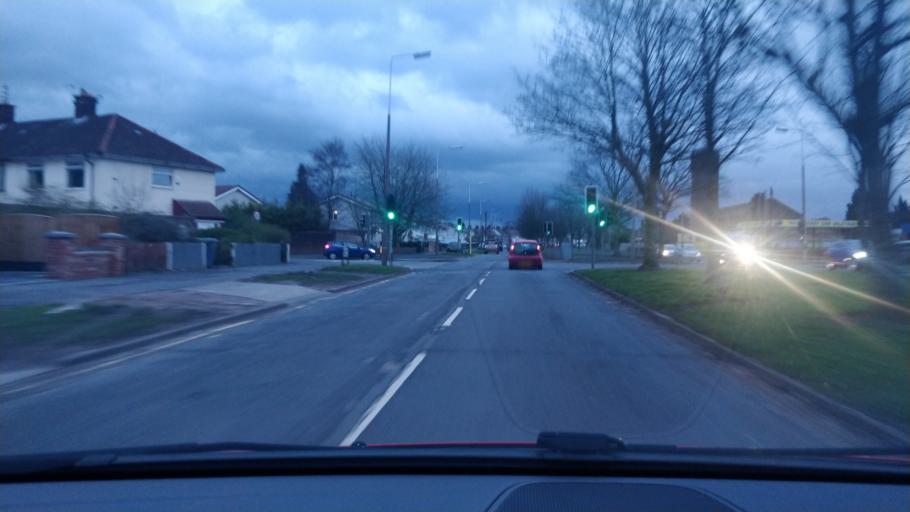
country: GB
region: England
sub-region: Knowsley
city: Knowsley
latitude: 53.4317
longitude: -2.8787
